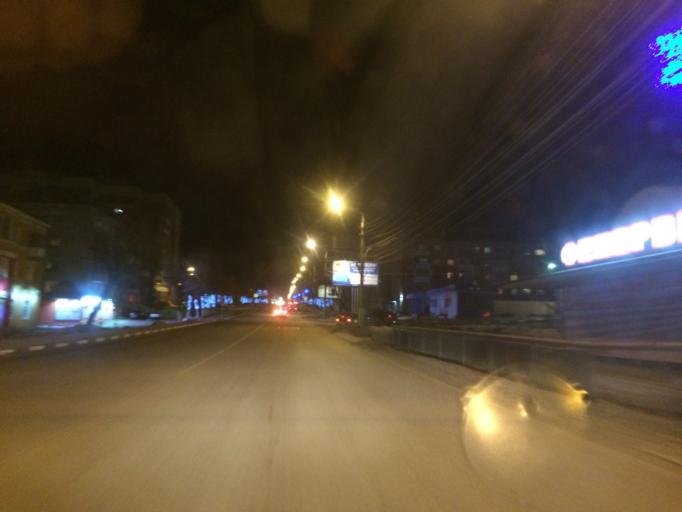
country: RU
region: Tula
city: Tula
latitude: 54.2043
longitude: 37.6780
